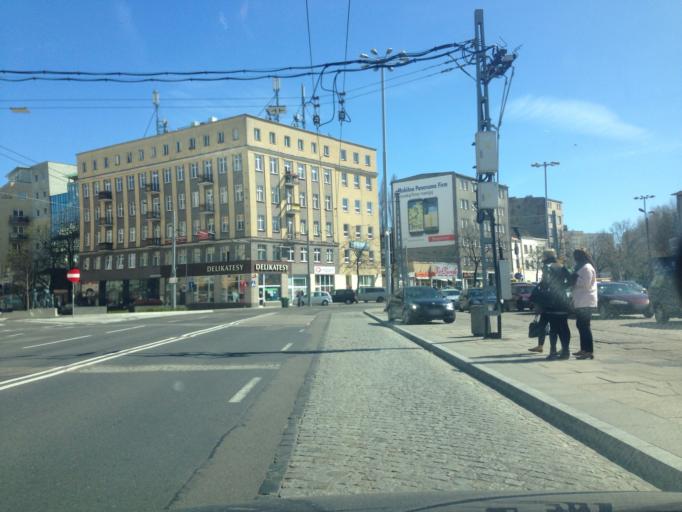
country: PL
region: Pomeranian Voivodeship
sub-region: Gdynia
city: Gdynia
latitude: 54.5211
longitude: 18.5313
